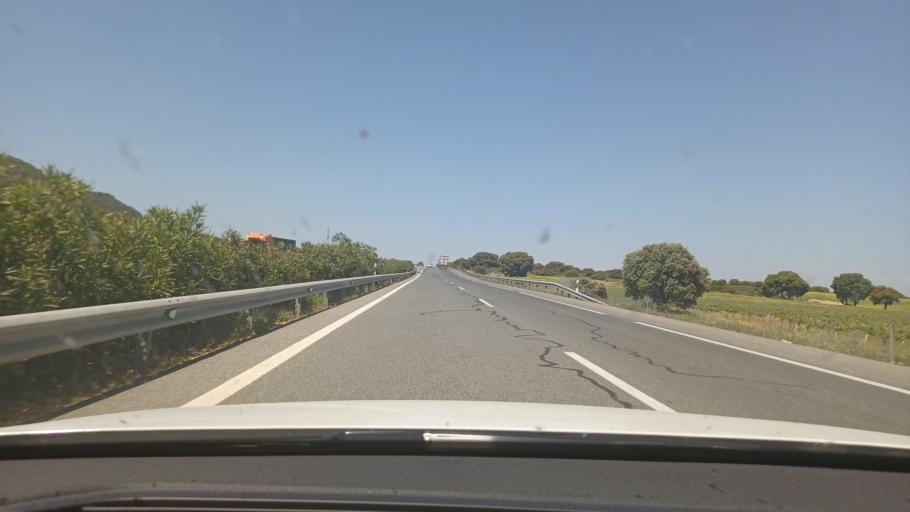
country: ES
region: Castille-La Mancha
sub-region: Provincia de Albacete
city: Corral-Rubio
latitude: 38.8996
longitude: -1.4612
